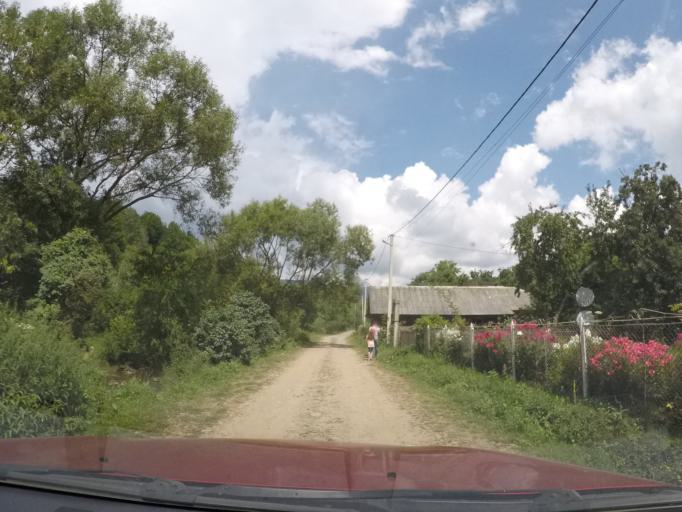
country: UA
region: Zakarpattia
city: Velykyi Bereznyi
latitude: 49.0369
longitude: 22.5816
